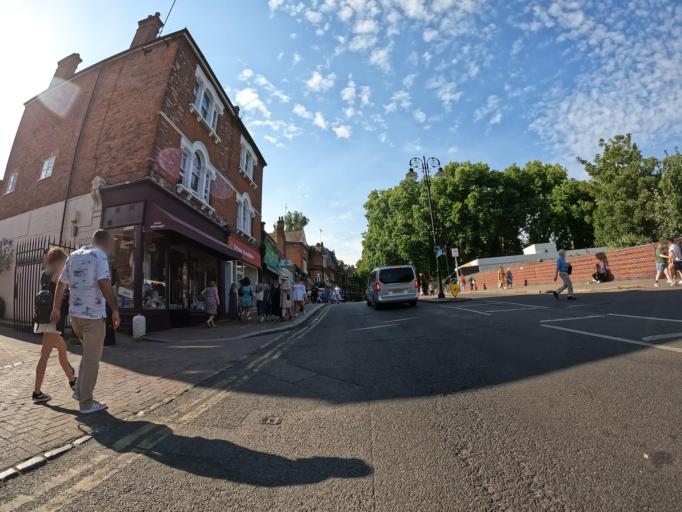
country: GB
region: England
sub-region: Greater London
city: Hendon
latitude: 51.6235
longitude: -0.2137
